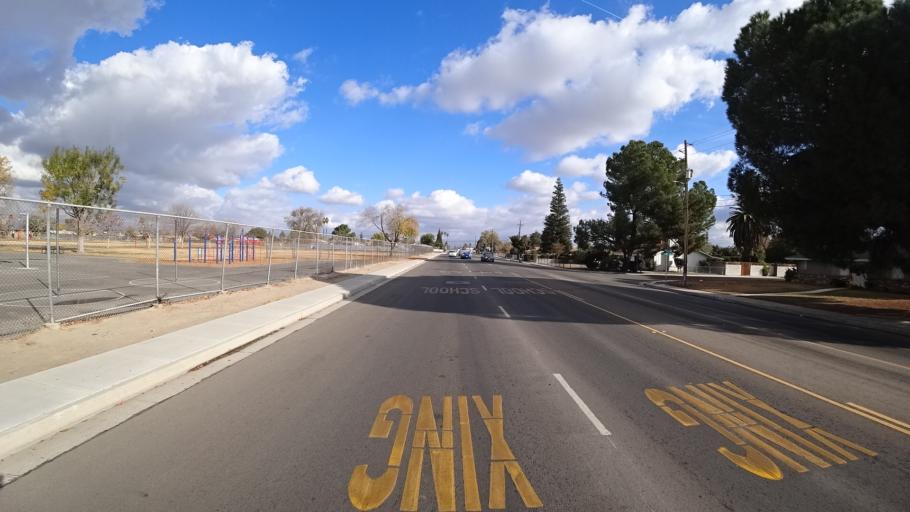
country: US
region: California
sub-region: Kern County
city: Bakersfield
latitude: 35.3323
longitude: -119.0274
